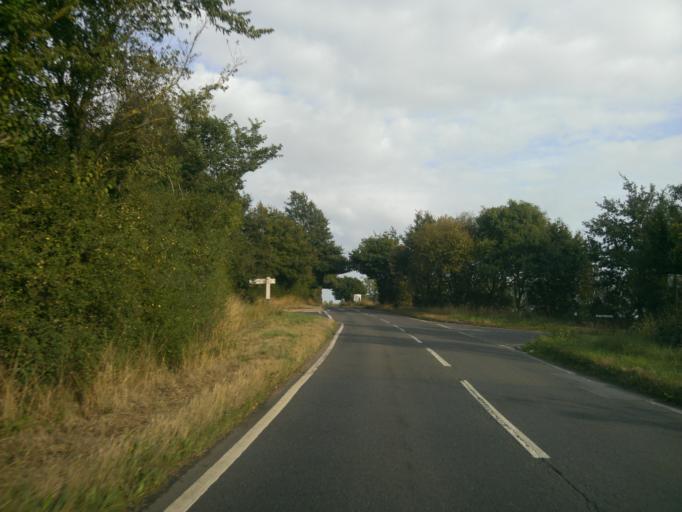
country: GB
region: England
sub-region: Essex
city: Great Totham
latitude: 51.7997
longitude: 0.7053
